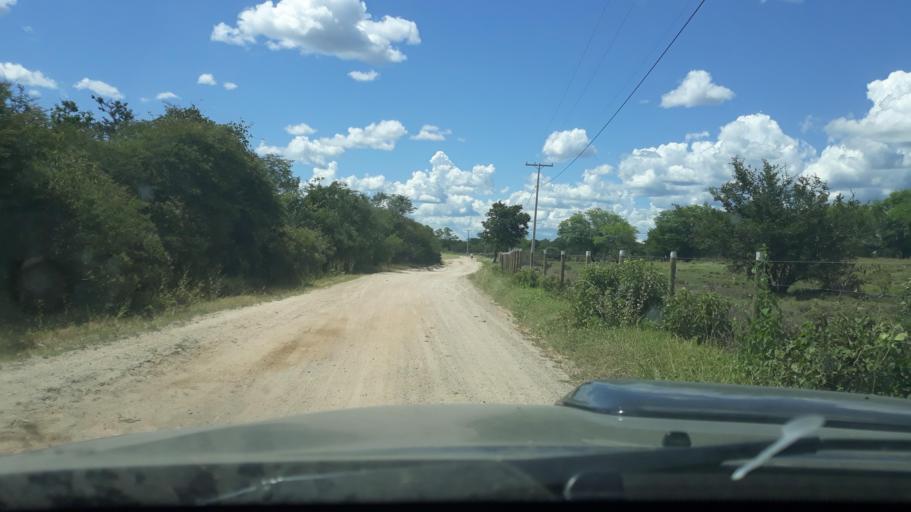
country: BR
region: Bahia
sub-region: Riacho De Santana
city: Riacho de Santana
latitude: -13.8808
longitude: -43.0211
